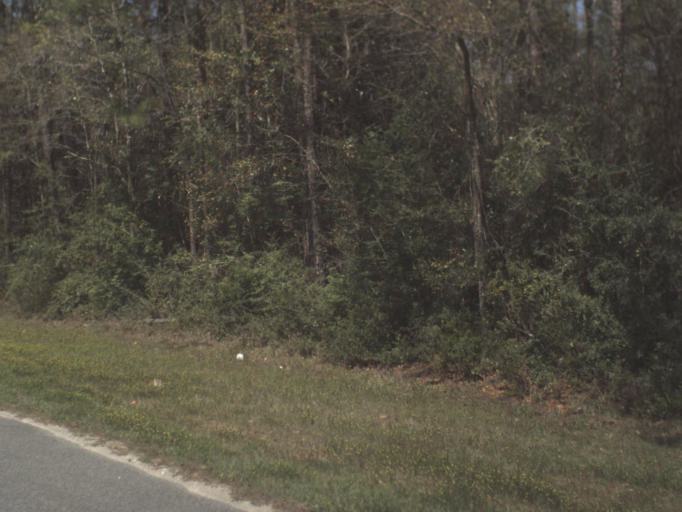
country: US
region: Florida
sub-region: Bay County
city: Lynn Haven
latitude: 30.3221
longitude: -85.6657
